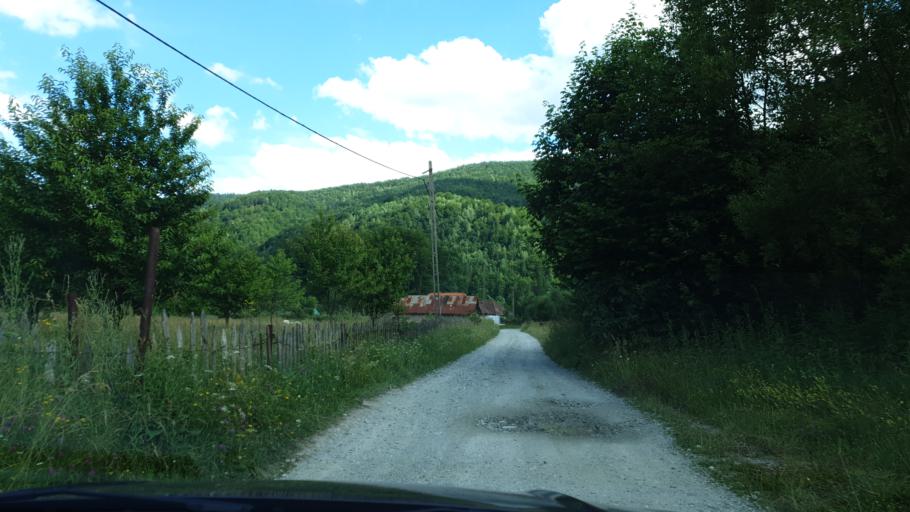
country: RO
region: Hunedoara
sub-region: Comuna Uricani
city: Uricani
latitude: 45.2987
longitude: 22.9937
